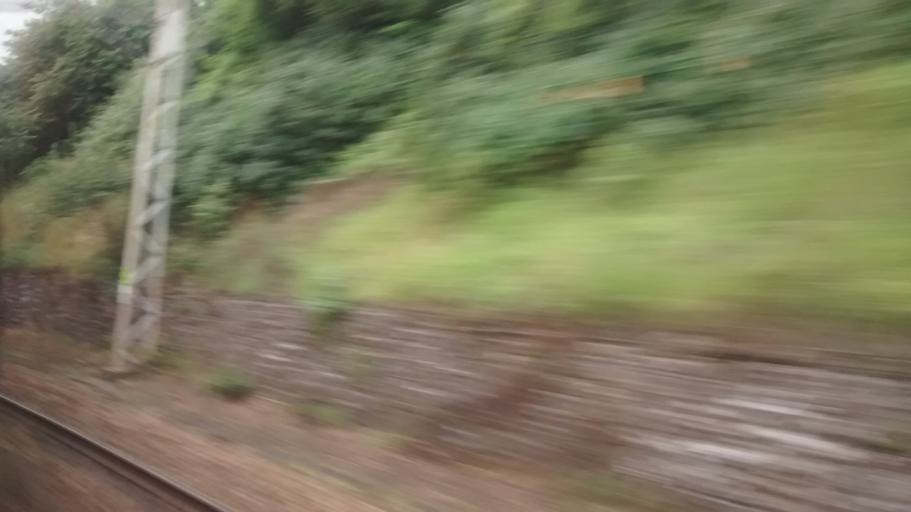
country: FR
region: Pays de la Loire
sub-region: Departement de la Sarthe
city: Change
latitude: 48.0043
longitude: 0.2575
